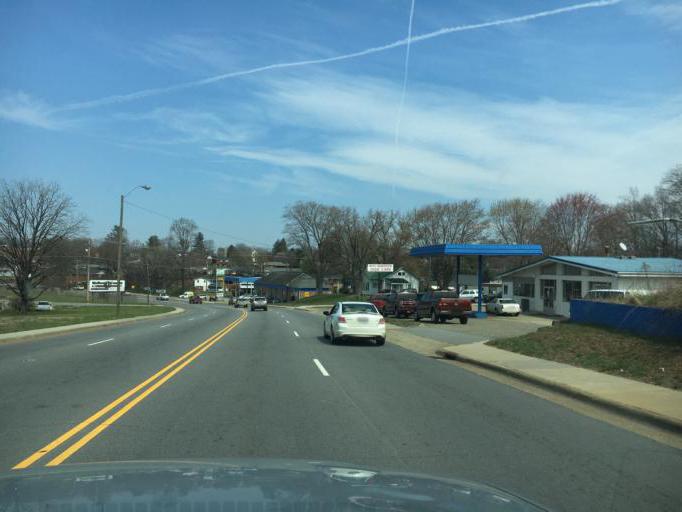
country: US
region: North Carolina
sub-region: McDowell County
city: Marion
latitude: 35.6768
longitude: -82.0127
